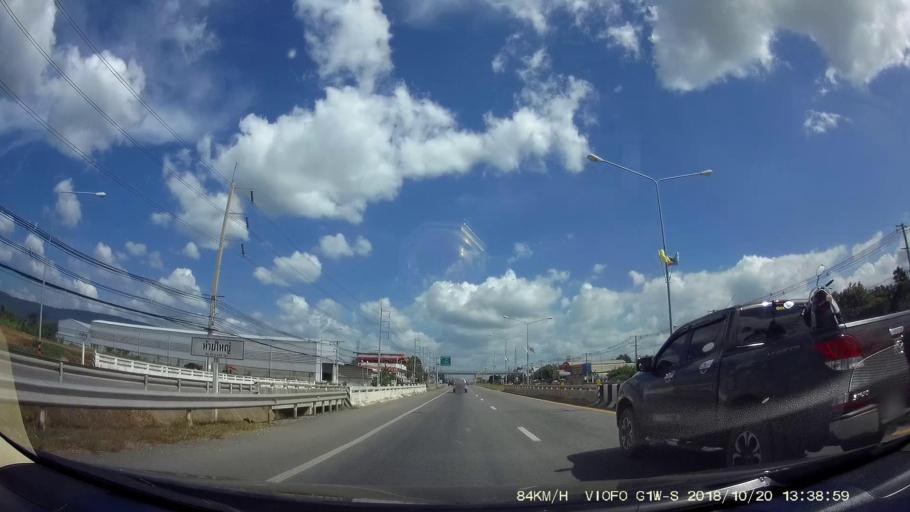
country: TH
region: Khon Kaen
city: Chum Phae
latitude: 16.5502
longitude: 102.0886
